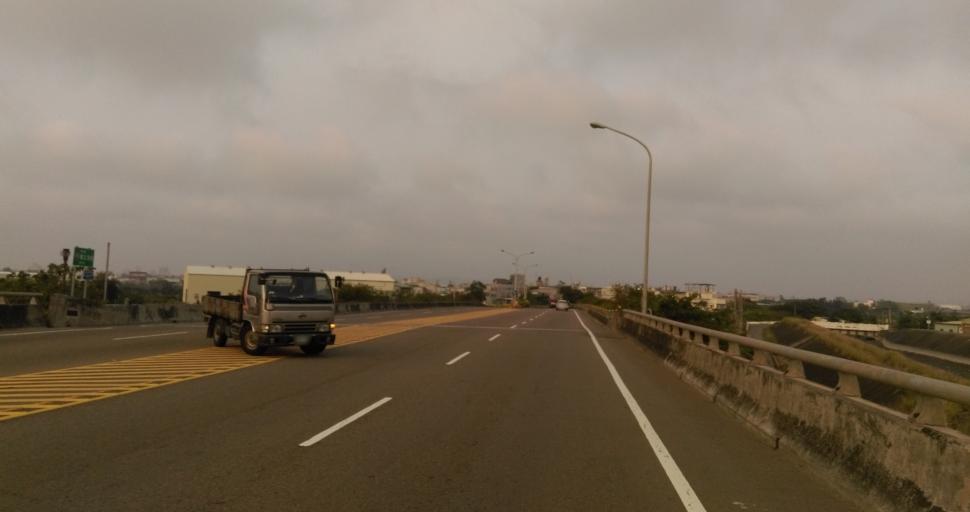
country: TW
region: Taiwan
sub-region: Hsinchu
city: Hsinchu
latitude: 24.8097
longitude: 120.9197
